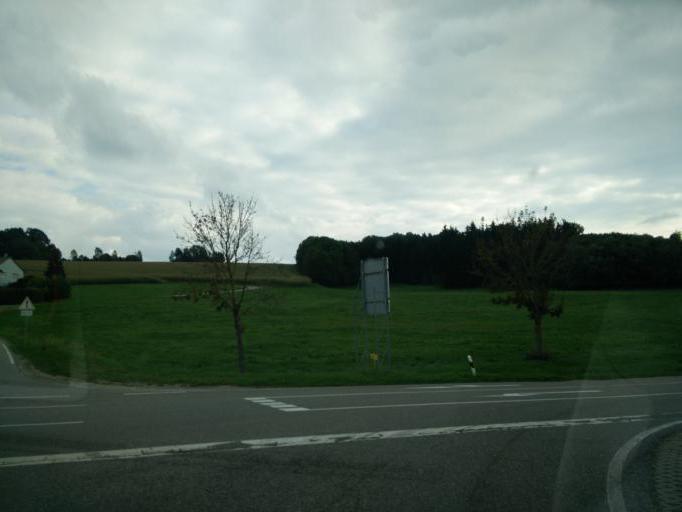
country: DE
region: Baden-Wuerttemberg
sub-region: Tuebingen Region
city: Bad Wurzach
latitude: 47.9090
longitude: 9.9133
